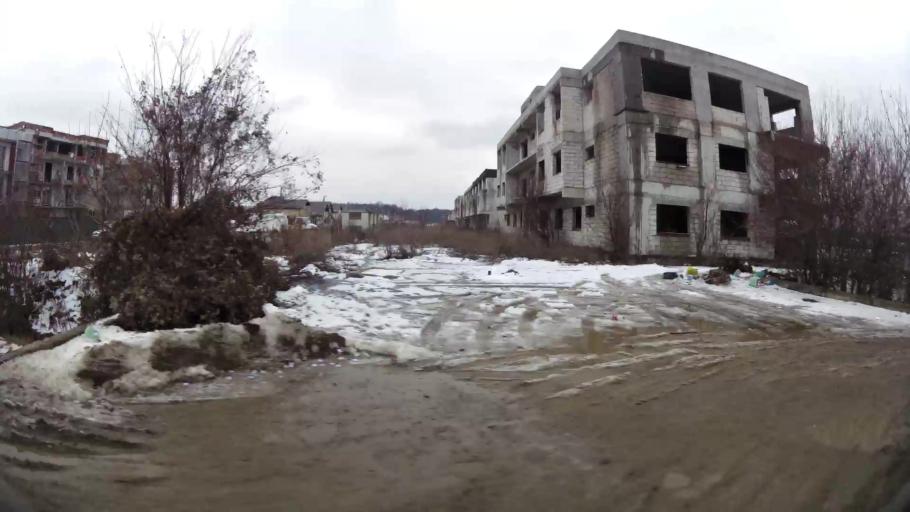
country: RO
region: Ilfov
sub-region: Comuna Tunari
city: Tunari
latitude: 44.5500
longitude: 26.1205
